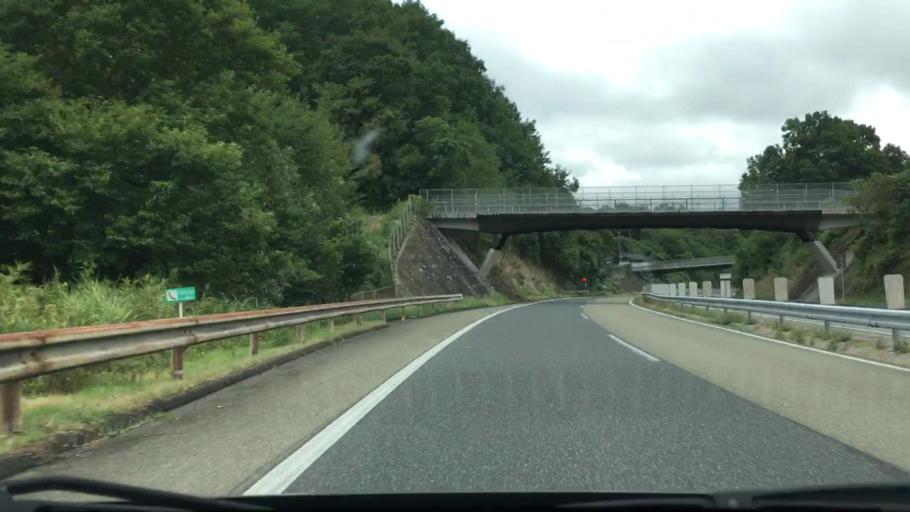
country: JP
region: Hiroshima
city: Shobara
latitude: 34.8285
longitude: 133.0496
